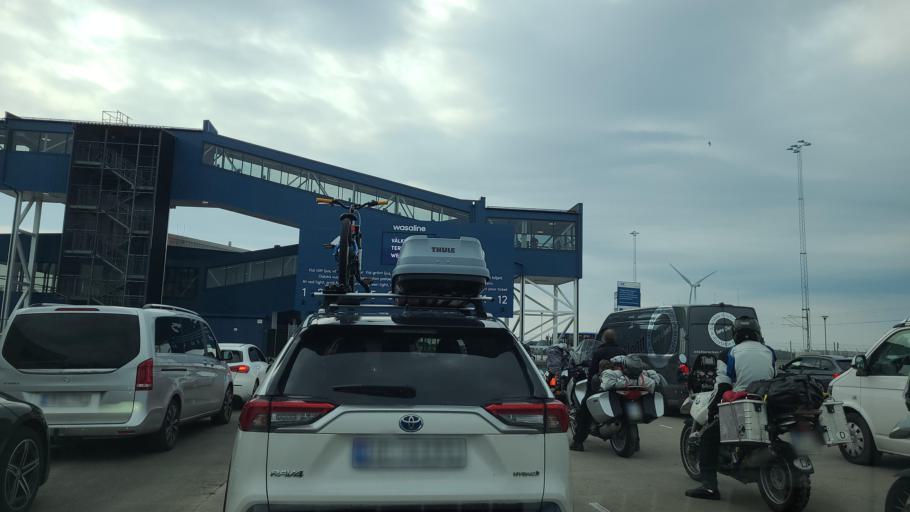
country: SE
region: Vaesterbotten
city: Obbola
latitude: 63.6819
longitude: 20.3395
